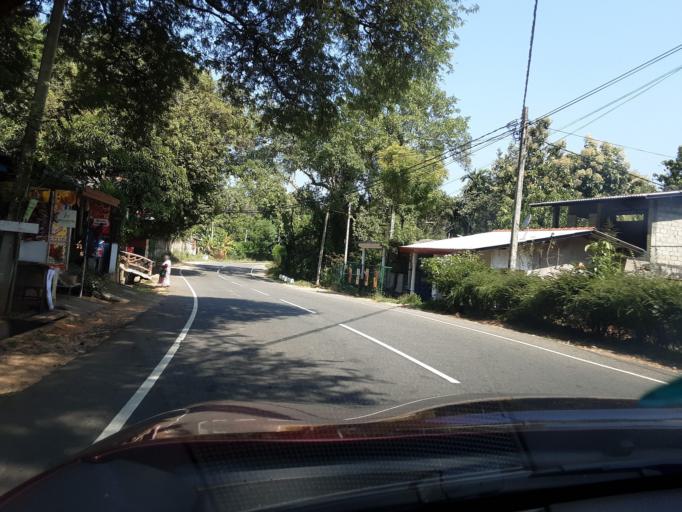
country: LK
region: Uva
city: Badulla
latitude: 7.1689
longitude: 81.0510
